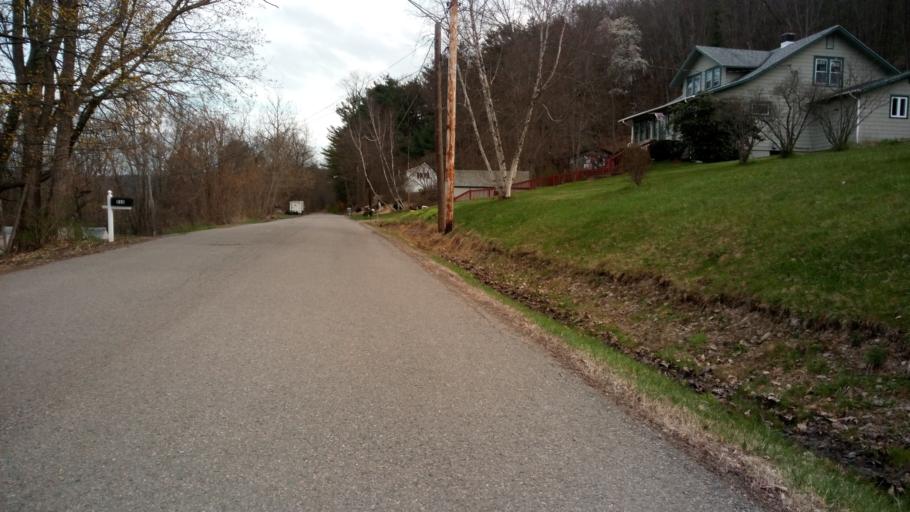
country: US
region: New York
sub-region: Chemung County
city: Southport
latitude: 42.0658
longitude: -76.8216
